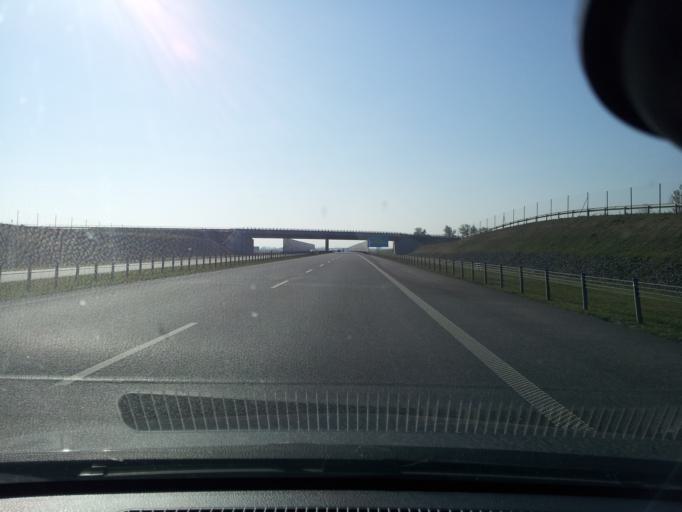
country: PL
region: Kujawsko-Pomorskie
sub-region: Powiat chelminski
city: Lisewo
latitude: 53.3093
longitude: 18.7060
